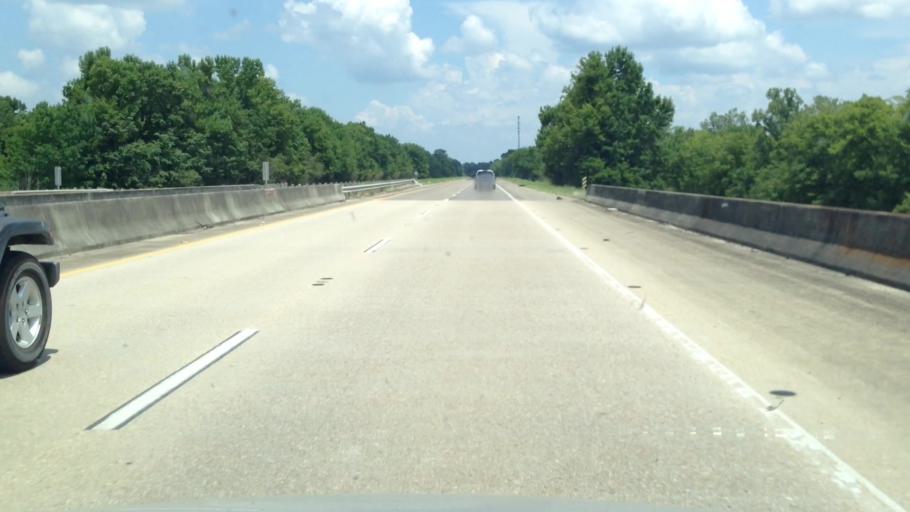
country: US
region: Louisiana
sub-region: Saint Landry Parish
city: Krotz Springs
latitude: 30.5410
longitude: -91.7825
